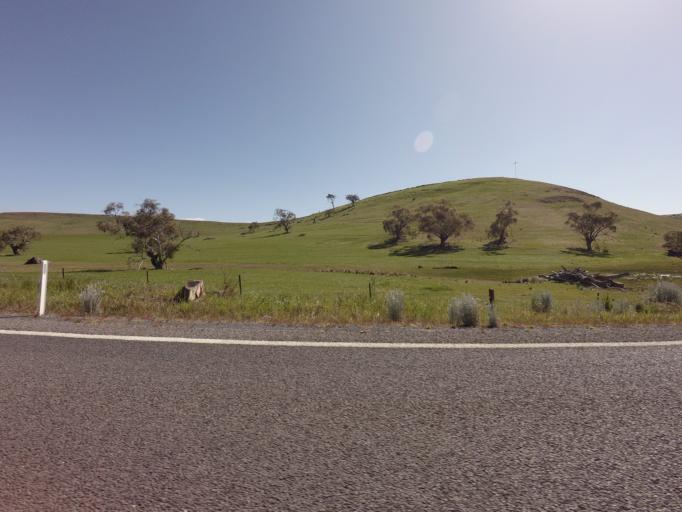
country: AU
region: Tasmania
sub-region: Derwent Valley
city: New Norfolk
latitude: -42.5746
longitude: 146.8822
